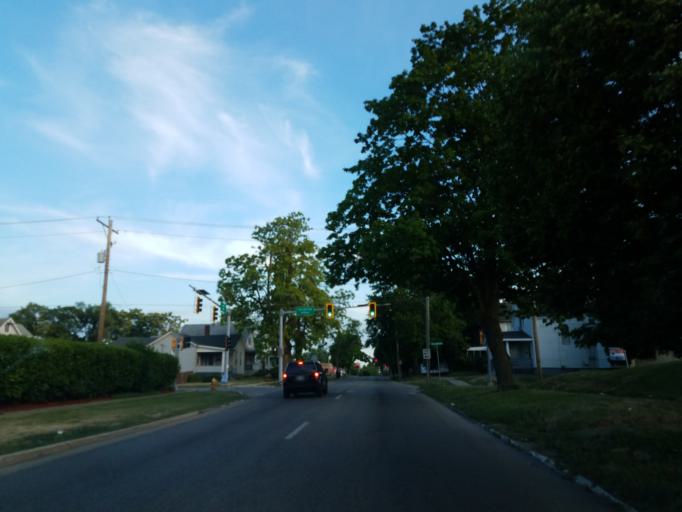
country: US
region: Illinois
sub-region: McLean County
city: Bloomington
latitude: 40.4733
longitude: -88.9943
